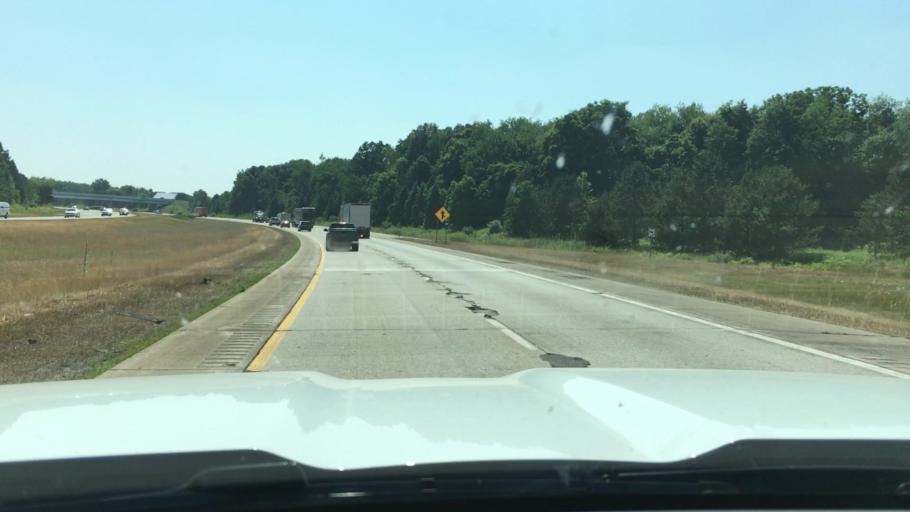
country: US
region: Michigan
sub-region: Clinton County
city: DeWitt
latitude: 42.8160
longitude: -84.5762
